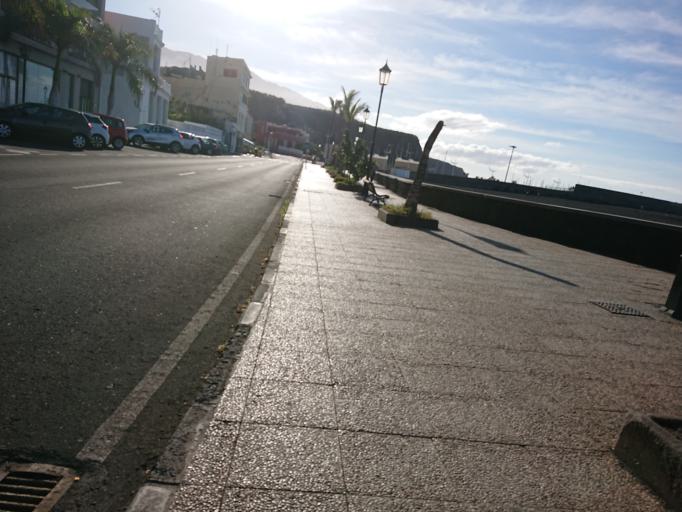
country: ES
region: Canary Islands
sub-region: Provincia de Santa Cruz de Tenerife
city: Tazacorte
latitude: 28.6488
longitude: -17.9448
